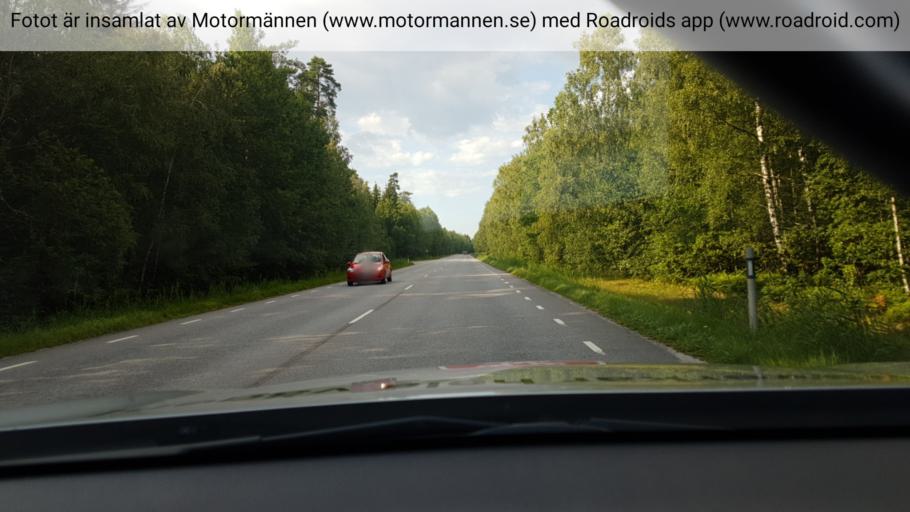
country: SE
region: Vaestra Goetaland
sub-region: Lidkopings Kommun
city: Lidkoping
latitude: 58.5270
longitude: 13.1117
